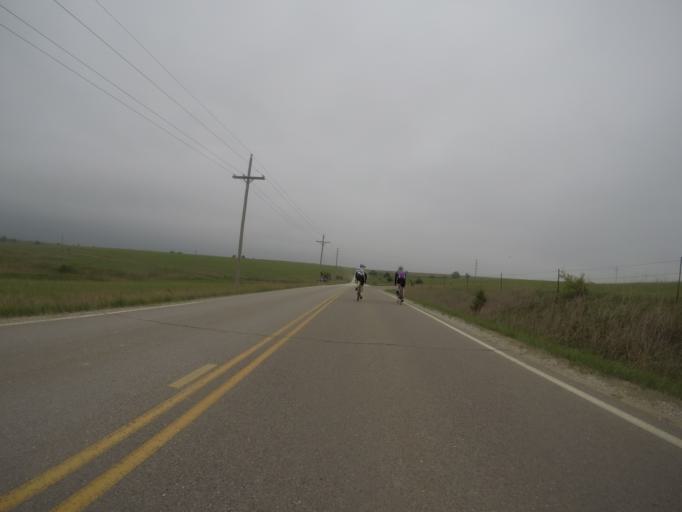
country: US
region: Kansas
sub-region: Pottawatomie County
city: Westmoreland
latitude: 39.5211
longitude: -96.3142
